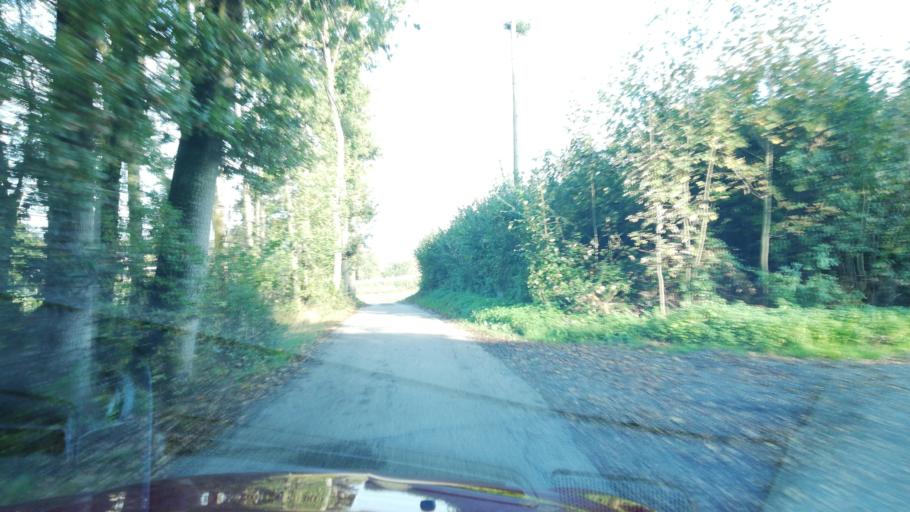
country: AT
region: Upper Austria
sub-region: Politischer Bezirk Grieskirchen
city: Bad Schallerbach
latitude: 48.2267
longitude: 13.9533
